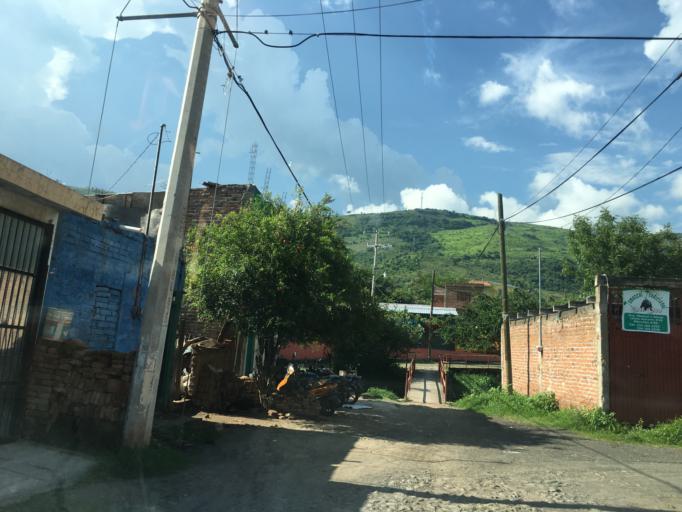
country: MX
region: Nayarit
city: Ixtlan del Rio
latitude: 21.0431
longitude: -104.3620
